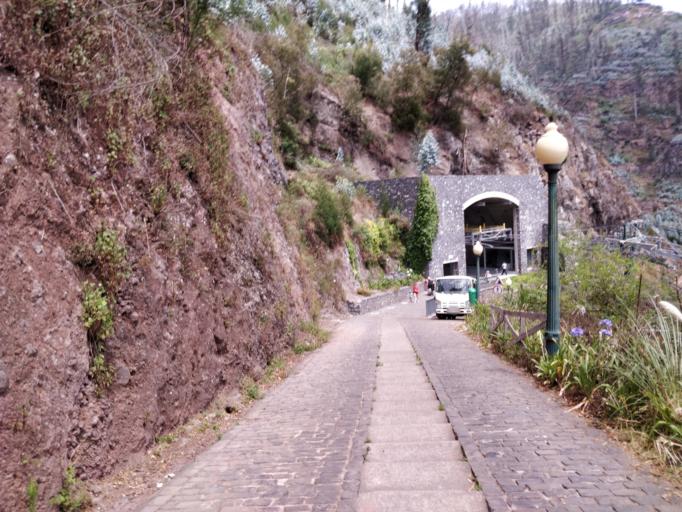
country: PT
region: Madeira
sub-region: Funchal
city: Nossa Senhora do Monte
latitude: 32.6772
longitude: -16.8984
